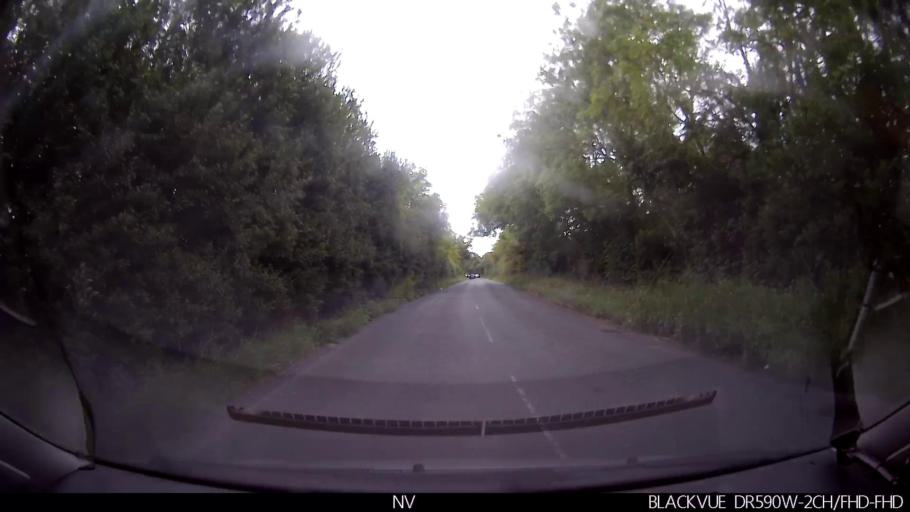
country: GB
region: England
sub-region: City of York
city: Holtby
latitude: 54.0463
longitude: -0.9592
